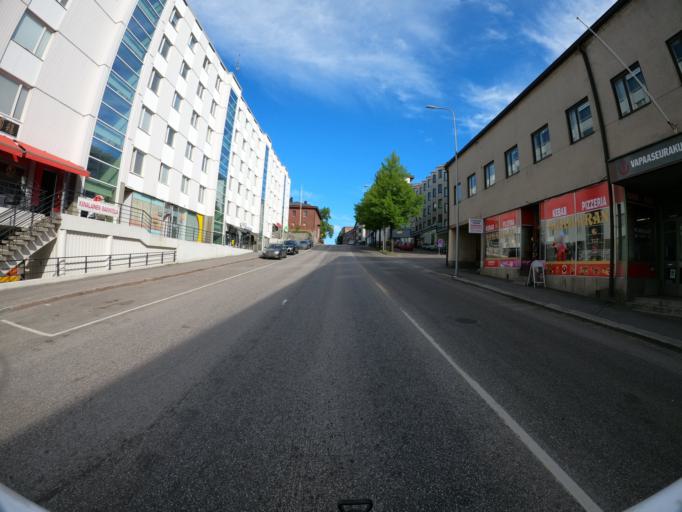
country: FI
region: Southern Savonia
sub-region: Savonlinna
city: Savonlinna
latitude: 61.8681
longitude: 28.8870
